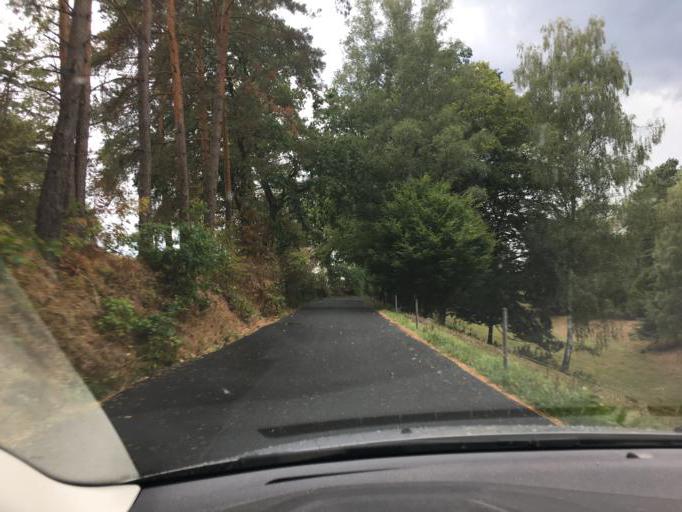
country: CZ
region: Ustecky
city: Benesov nad Ploucnici
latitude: 50.8159
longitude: 14.3402
